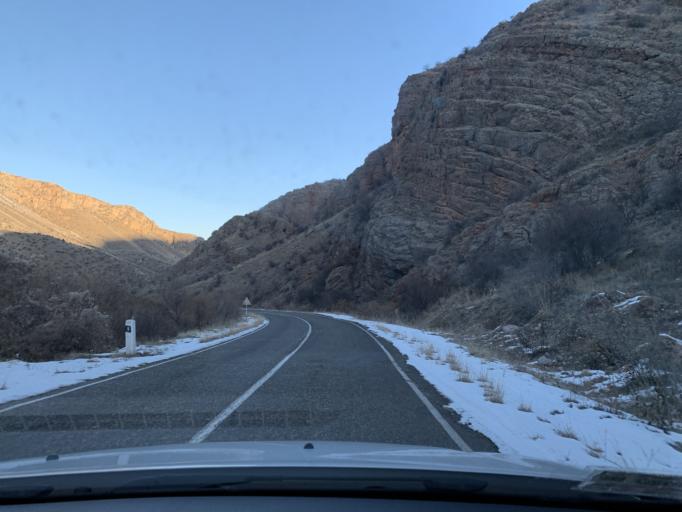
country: AM
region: Vayots' Dzori Marz
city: Areni
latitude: 39.6931
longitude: 45.2148
